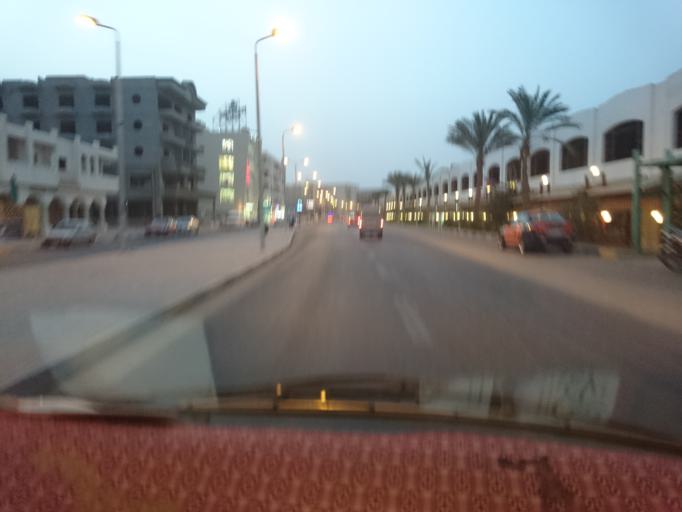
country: EG
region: Red Sea
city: Hurghada
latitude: 27.2388
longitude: 33.8456
